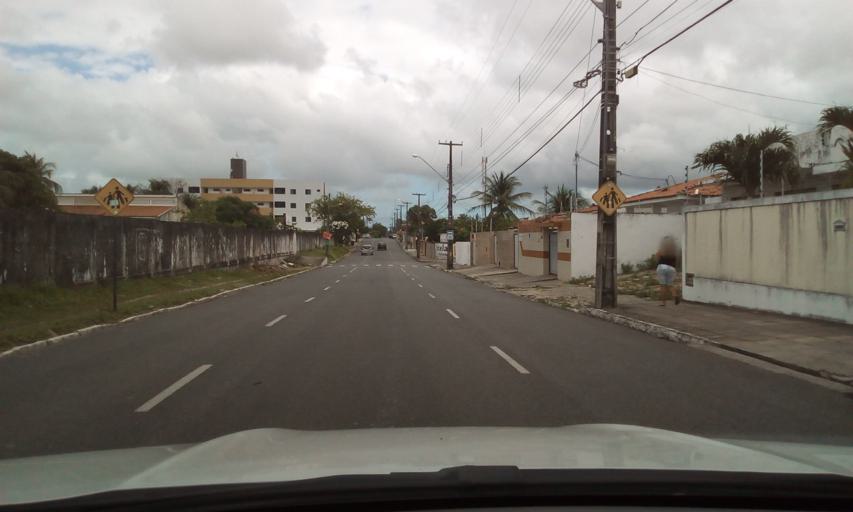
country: BR
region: Paraiba
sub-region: Joao Pessoa
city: Joao Pessoa
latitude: -7.1585
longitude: -34.8741
